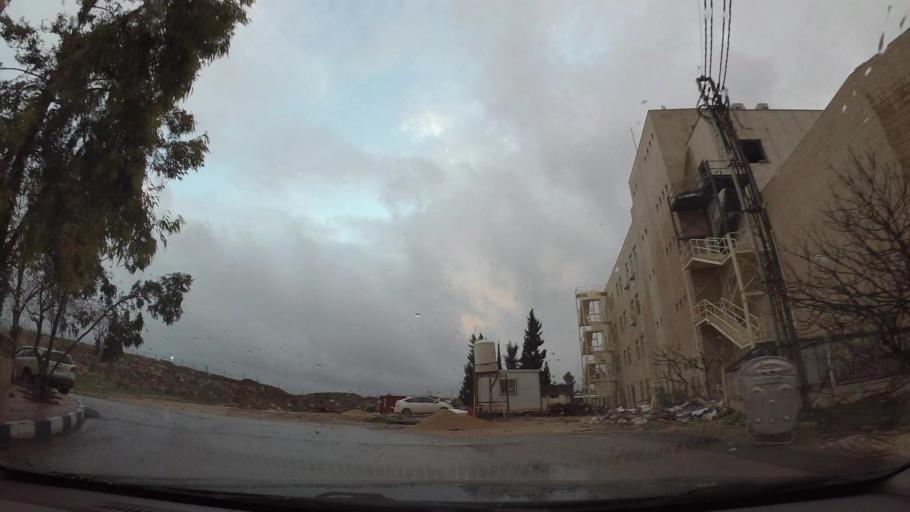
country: JO
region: Amman
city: Amman
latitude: 31.9987
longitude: 35.9199
